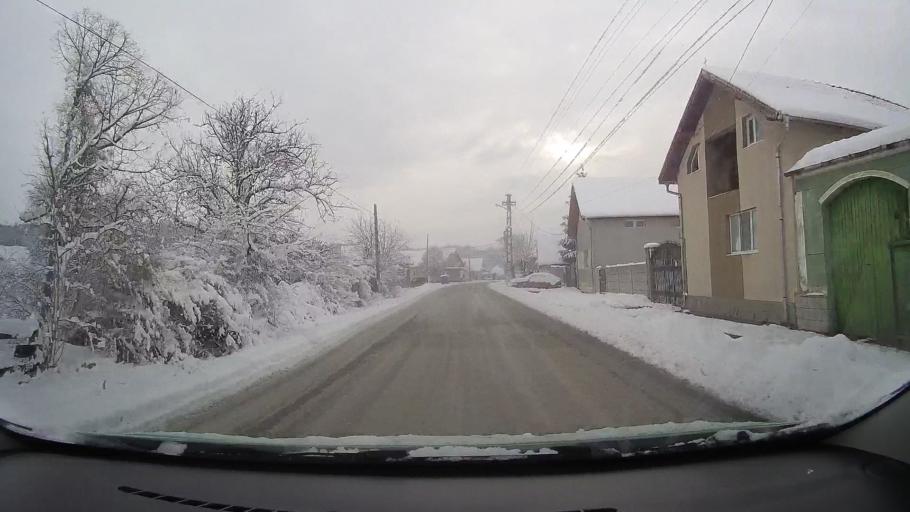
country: RO
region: Alba
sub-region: Comuna Pianu
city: Pianu de Jos
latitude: 45.9418
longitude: 23.4832
